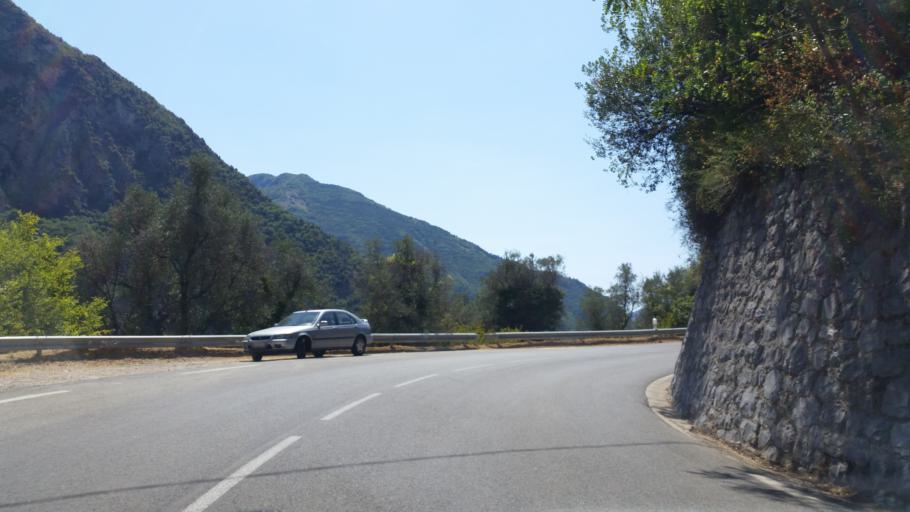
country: FR
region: Provence-Alpes-Cote d'Azur
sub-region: Departement des Alpes-Maritimes
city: Breil-sur-Roya
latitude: 43.9485
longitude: 7.5125
